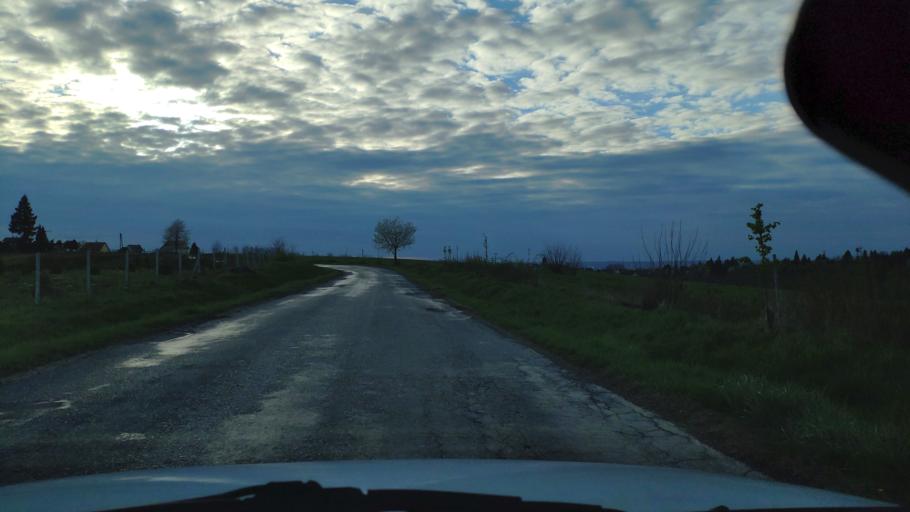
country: HU
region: Zala
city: Nagykanizsa
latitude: 46.4301
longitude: 17.0515
